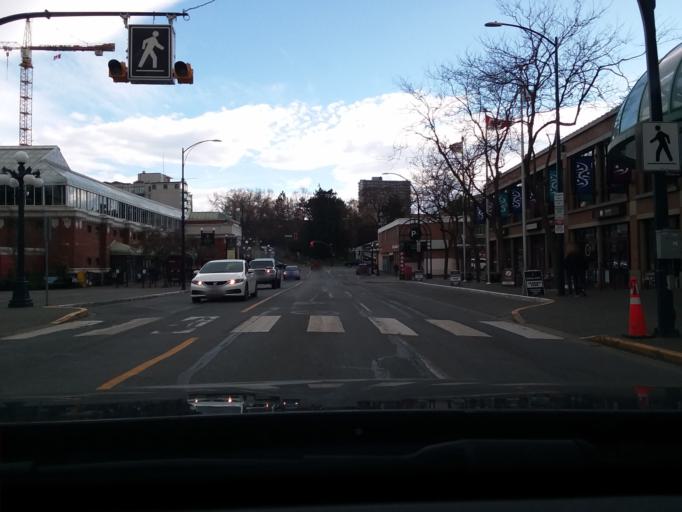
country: CA
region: British Columbia
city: Victoria
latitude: 48.4215
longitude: -123.3661
